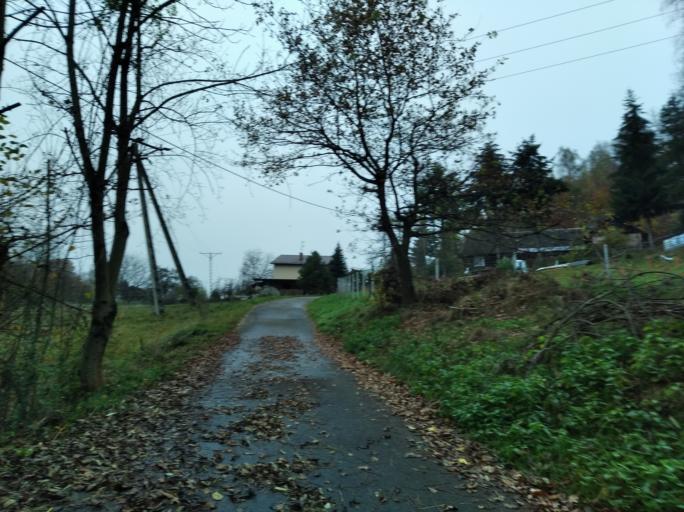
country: PL
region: Subcarpathian Voivodeship
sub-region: Powiat krosnienski
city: Korczyna
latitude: 49.7411
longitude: 21.7899
